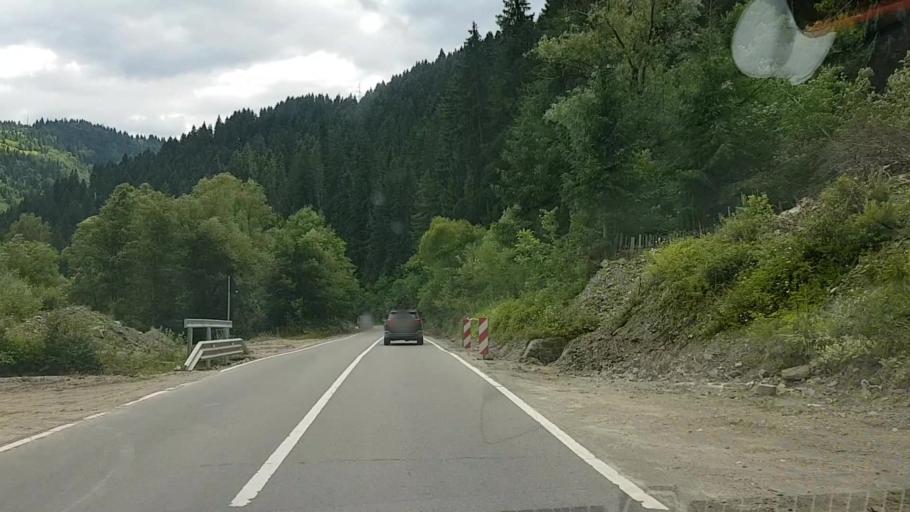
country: RO
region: Neamt
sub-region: Comuna Farcasa
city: Farcasa
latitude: 47.1403
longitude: 25.8594
